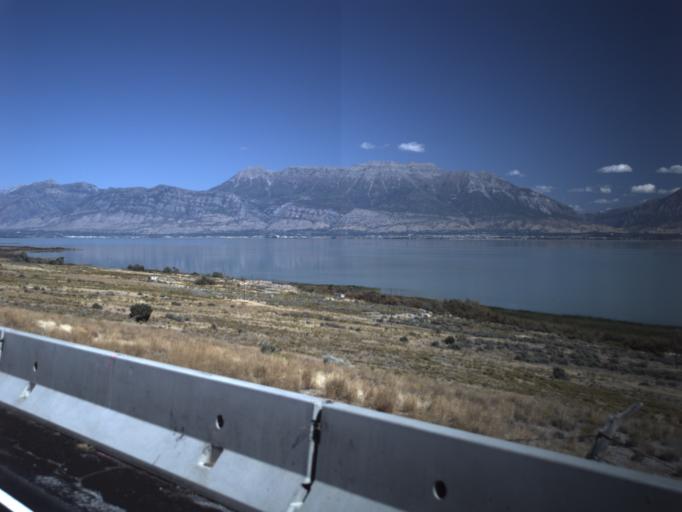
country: US
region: Utah
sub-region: Utah County
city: Saratoga Springs
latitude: 40.2308
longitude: -111.8704
